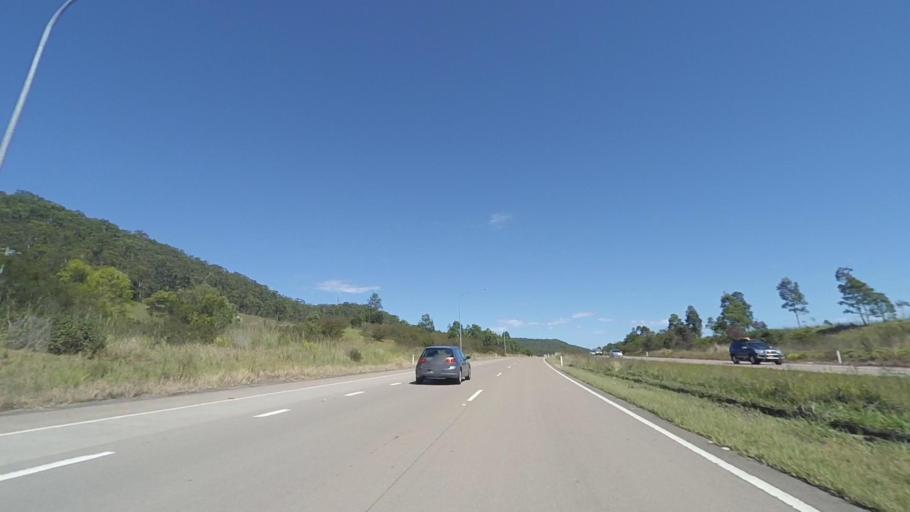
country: AU
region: New South Wales
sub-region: Port Stephens Shire
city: Port Stephens
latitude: -32.6296
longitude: 151.9915
